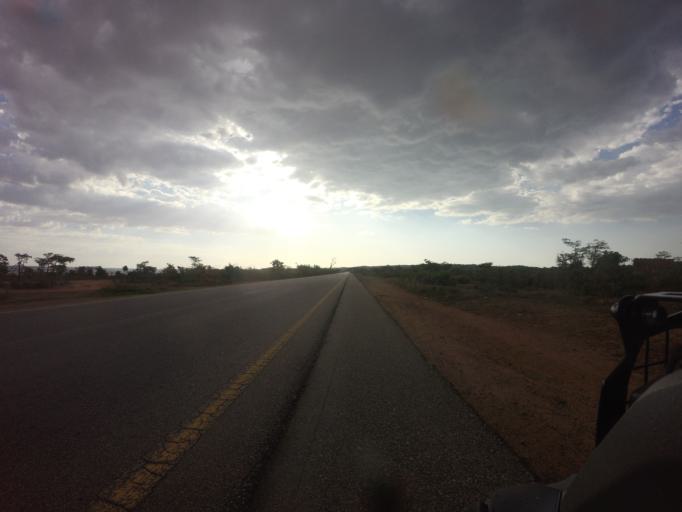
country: AO
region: Huila
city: Lubango
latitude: -14.6055
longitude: 13.9927
